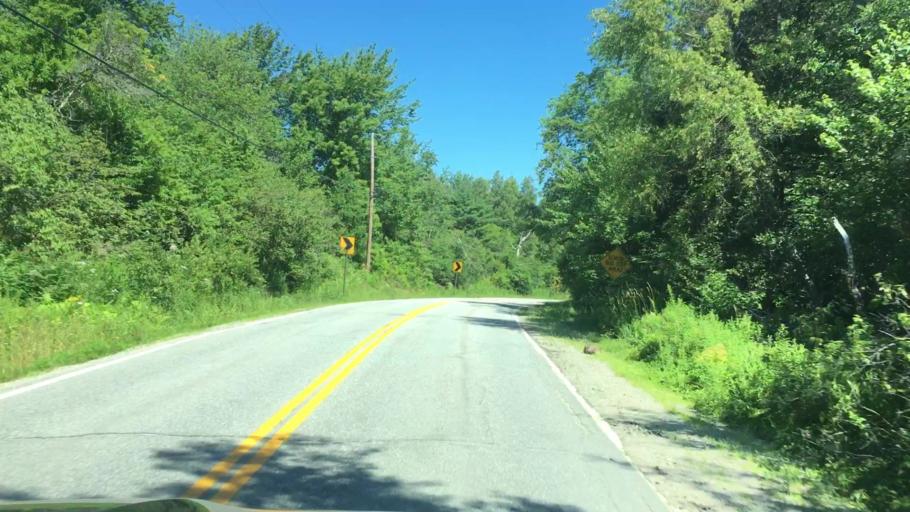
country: US
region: Maine
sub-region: Hancock County
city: Penobscot
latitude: 44.4985
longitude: -68.6815
